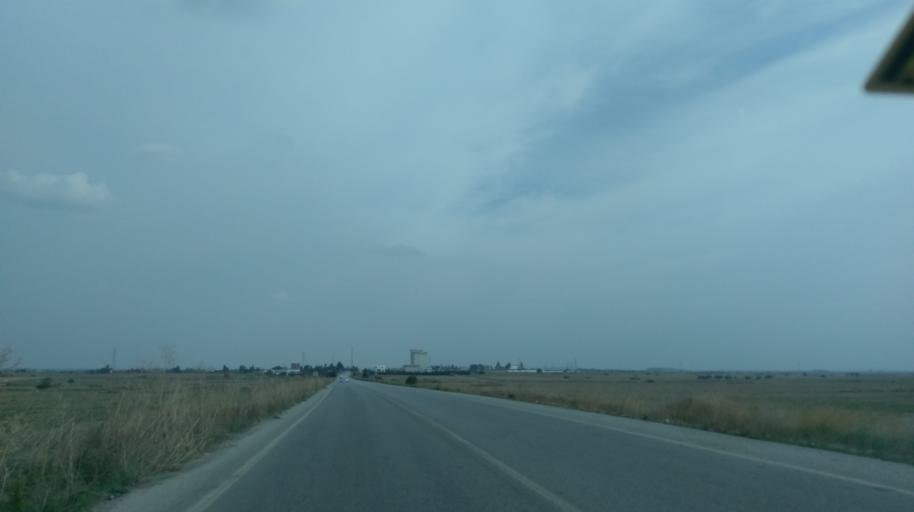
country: CY
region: Ammochostos
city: Lefkonoiko
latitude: 35.2566
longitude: 33.7078
